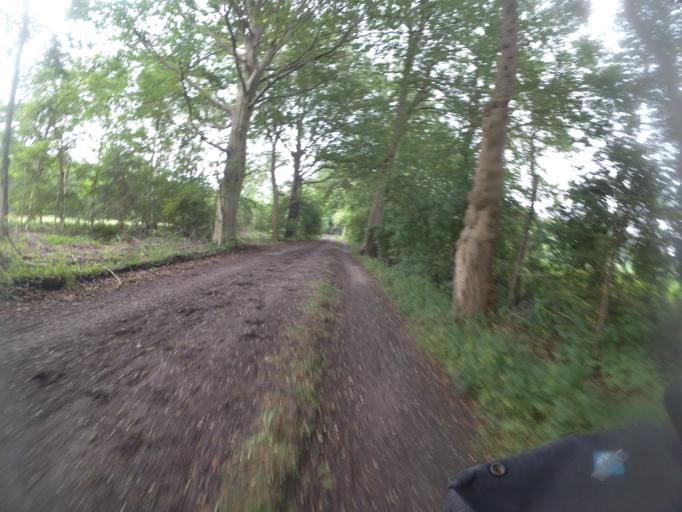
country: NL
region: Drenthe
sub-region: Gemeente Westerveld
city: Dwingeloo
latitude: 52.8117
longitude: 6.3494
